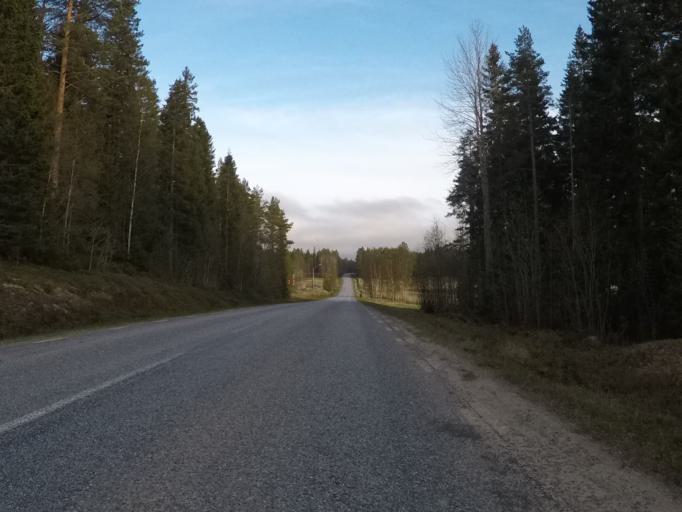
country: SE
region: Vaesterbotten
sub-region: Robertsfors Kommun
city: Robertsfors
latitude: 63.9901
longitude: 20.8109
